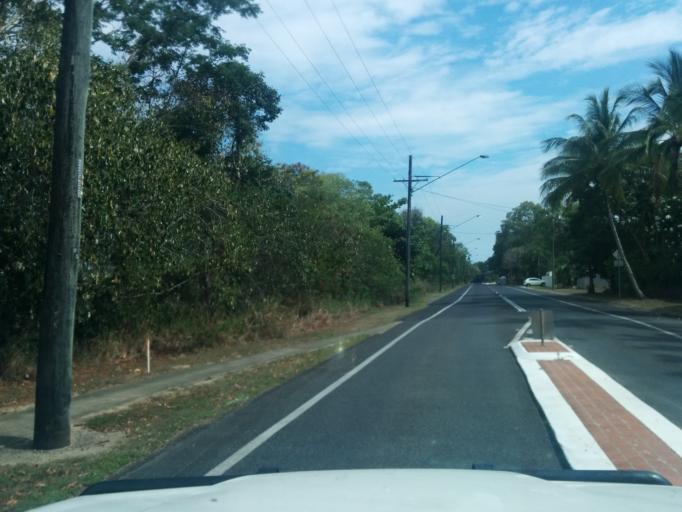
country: AU
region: Queensland
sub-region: Cairns
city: Yorkeys Knob
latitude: -16.8451
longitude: 145.7351
